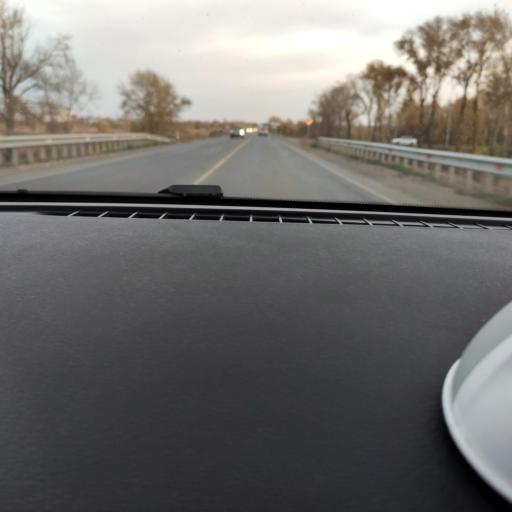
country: RU
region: Samara
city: Samara
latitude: 53.1002
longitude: 50.1420
